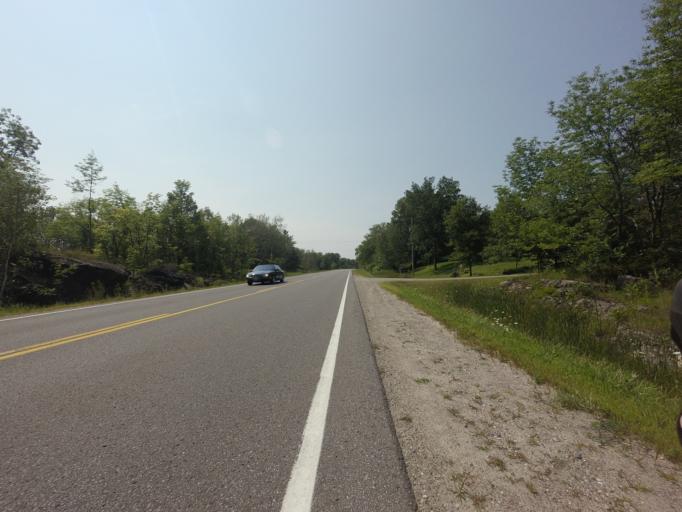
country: CA
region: Ontario
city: Kingston
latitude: 44.6593
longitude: -76.6900
